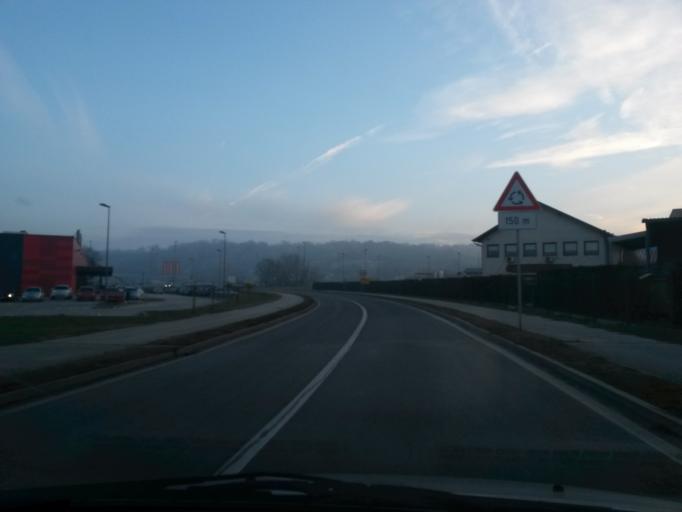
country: HR
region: Varazdinska
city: Ludbreg
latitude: 46.2436
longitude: 16.6286
